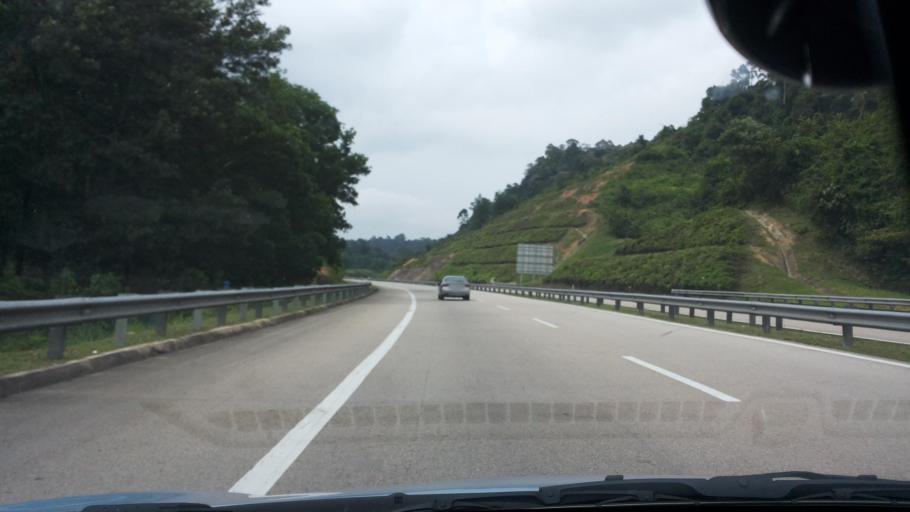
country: MY
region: Pahang
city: Kuantan
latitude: 3.7540
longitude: 103.1296
